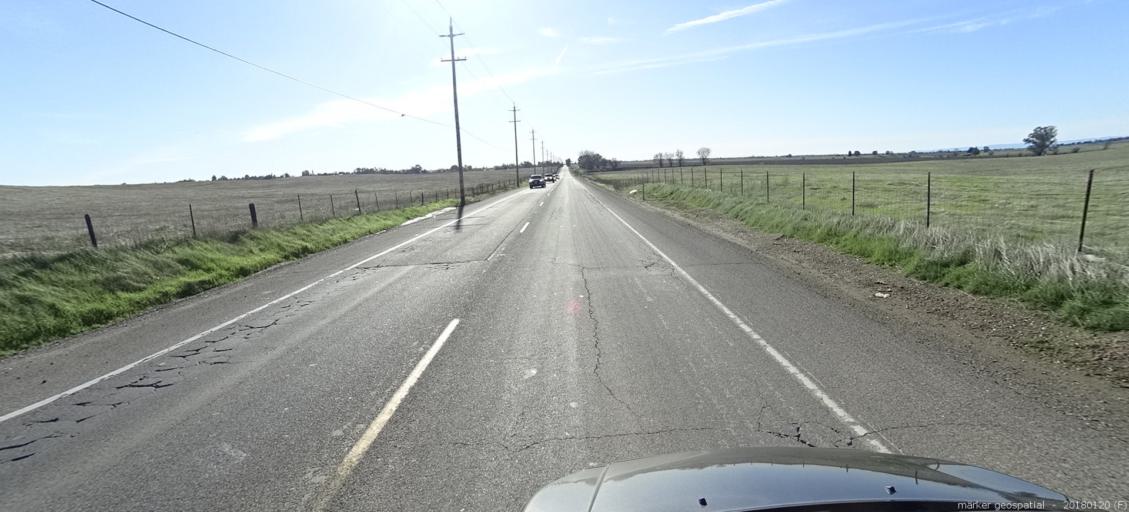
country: US
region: California
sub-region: Sacramento County
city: Rancho Murieta
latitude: 38.5154
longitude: -121.2083
